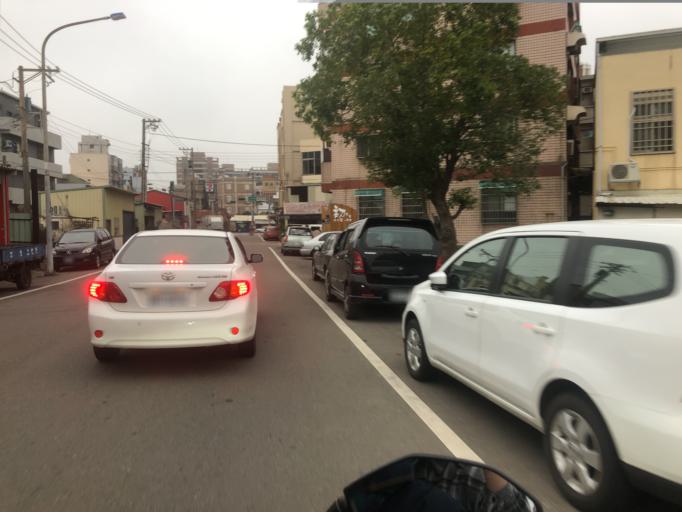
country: TW
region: Taiwan
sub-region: Hsinchu
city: Hsinchu
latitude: 24.7989
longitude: 120.9428
